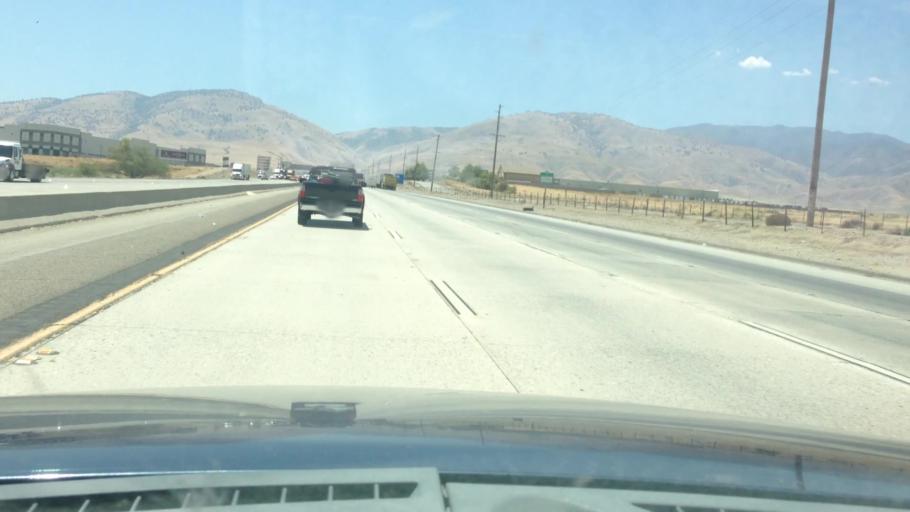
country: US
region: California
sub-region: Kern County
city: Frazier Park
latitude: 34.9991
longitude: -118.9494
